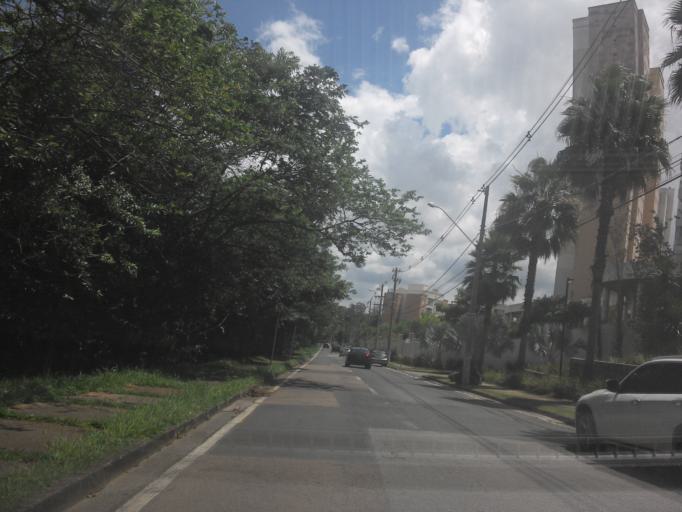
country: BR
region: Sao Paulo
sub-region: Campinas
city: Campinas
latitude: -22.8658
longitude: -47.0244
